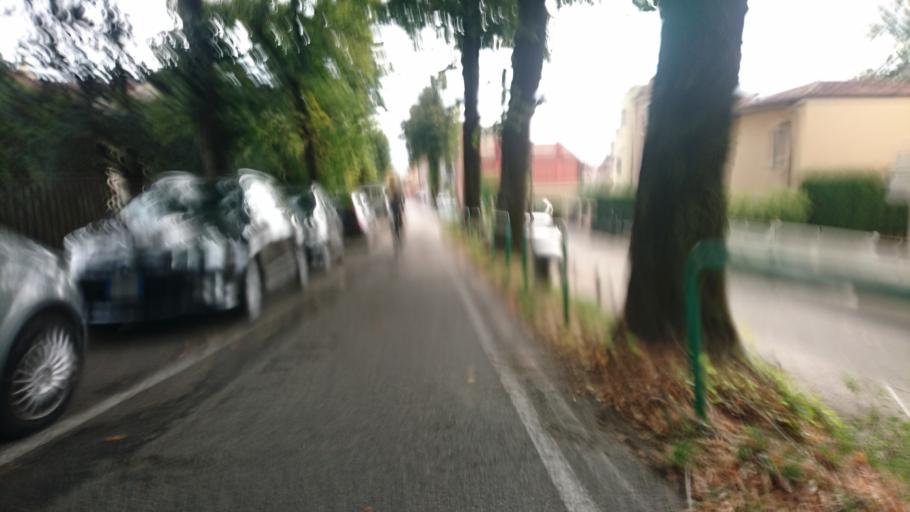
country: IT
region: Veneto
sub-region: Provincia di Padova
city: Padova
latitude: 45.4101
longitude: 11.8560
